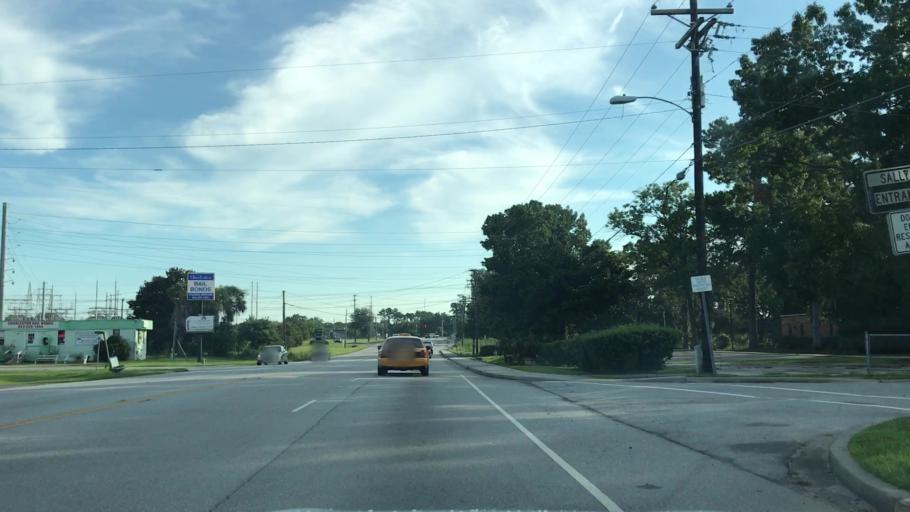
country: US
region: South Carolina
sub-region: Charleston County
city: North Charleston
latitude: 32.8473
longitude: -80.0143
